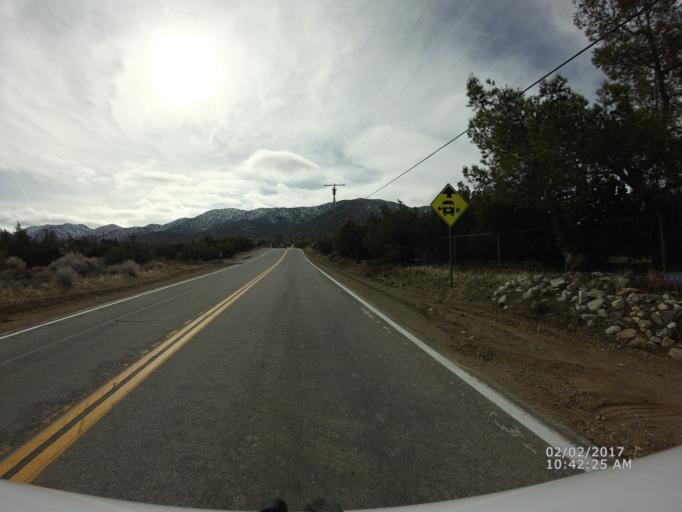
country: US
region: California
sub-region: Los Angeles County
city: Littlerock
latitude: 34.4473
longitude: -117.9360
